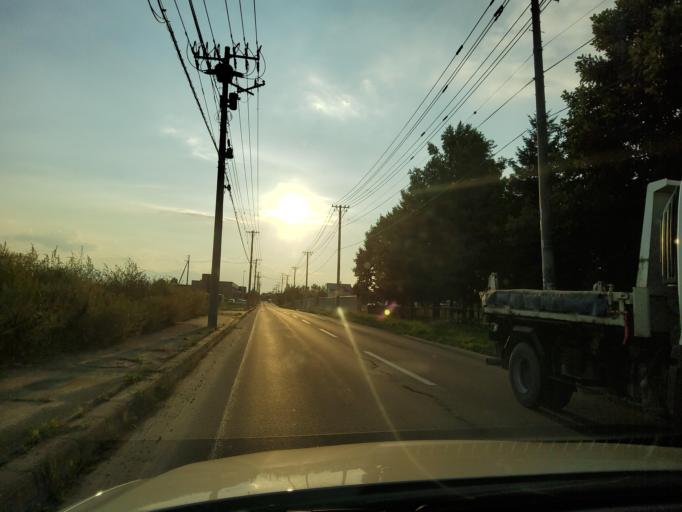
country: JP
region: Hokkaido
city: Obihiro
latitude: 42.9386
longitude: 143.1546
